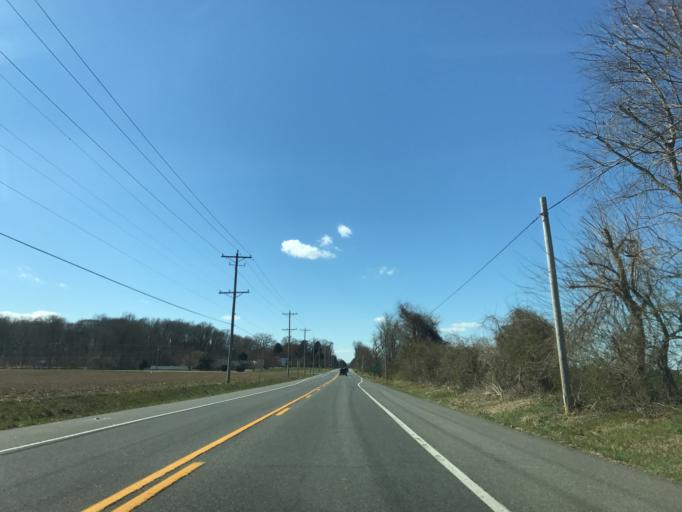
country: US
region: Maryland
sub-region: Kent County
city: Chestertown
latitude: 39.2144
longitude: -76.1108
